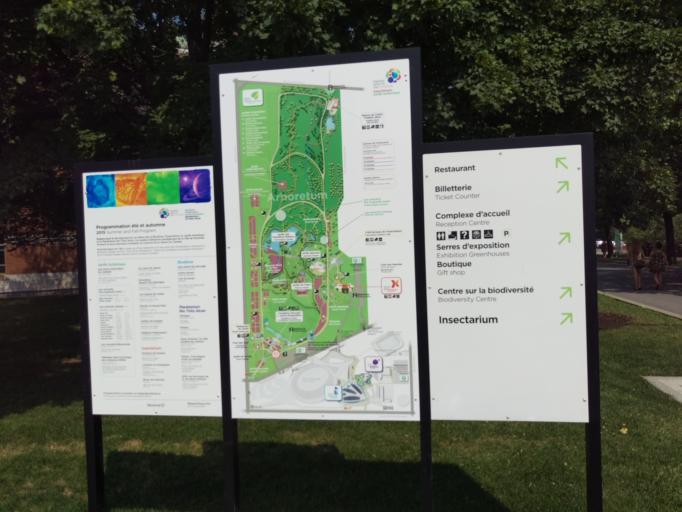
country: CA
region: Quebec
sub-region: Monteregie
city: Longueuil
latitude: 45.5565
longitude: -73.5557
